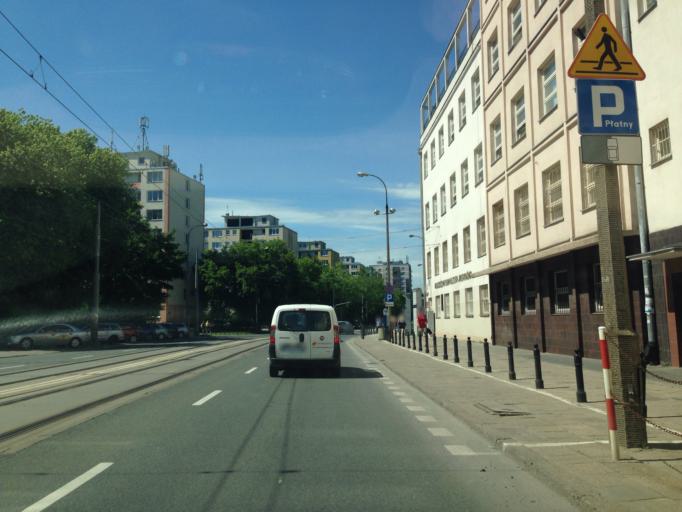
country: PL
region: Masovian Voivodeship
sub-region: Warszawa
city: Wola
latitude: 52.2526
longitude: 20.9899
